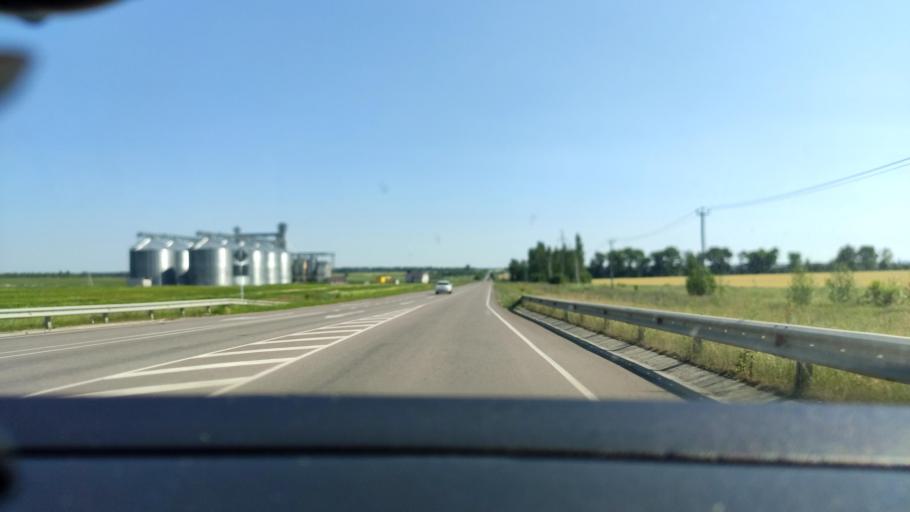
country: RU
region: Voronezj
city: Novaya Usman'
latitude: 51.5860
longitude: 39.3747
